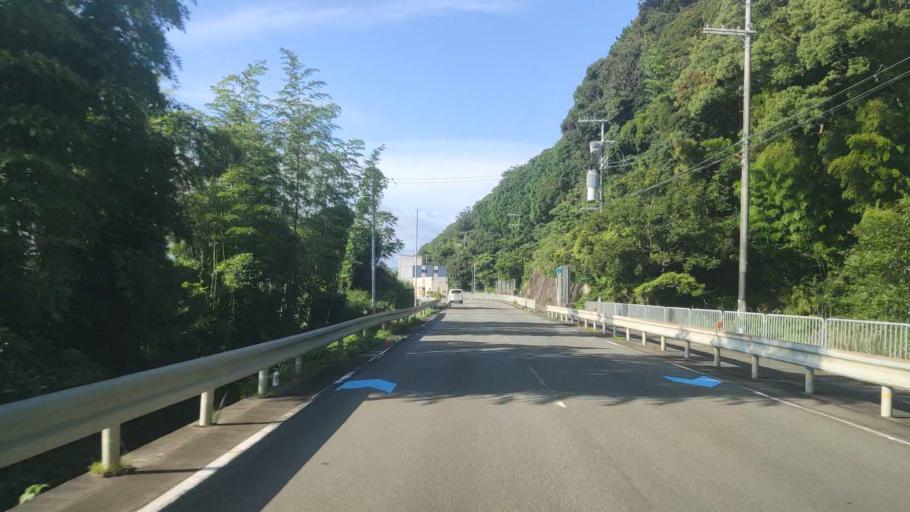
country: JP
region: Wakayama
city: Tanabe
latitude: 33.6679
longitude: 135.4079
